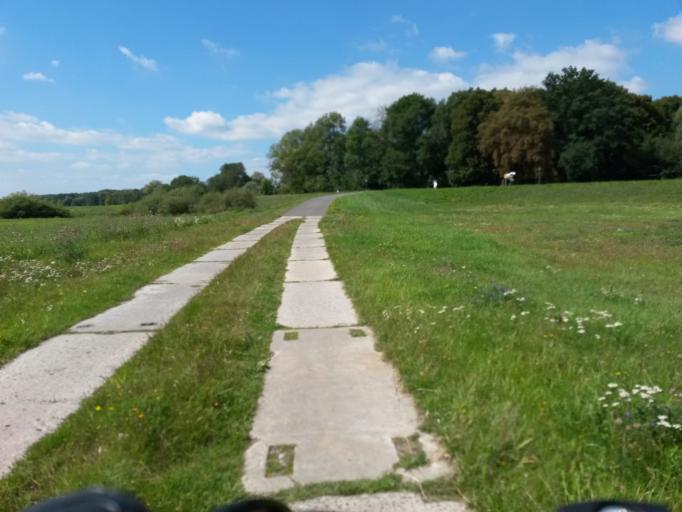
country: DE
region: Brandenburg
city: Meyenburg
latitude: 53.0095
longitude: 14.2296
